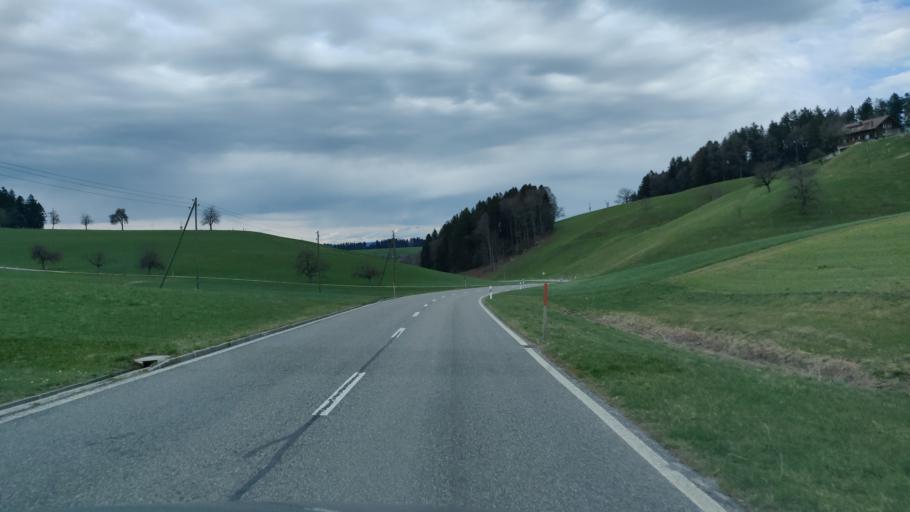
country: CH
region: Bern
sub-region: Emmental District
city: Durrenroth
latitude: 47.0997
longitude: 7.7764
